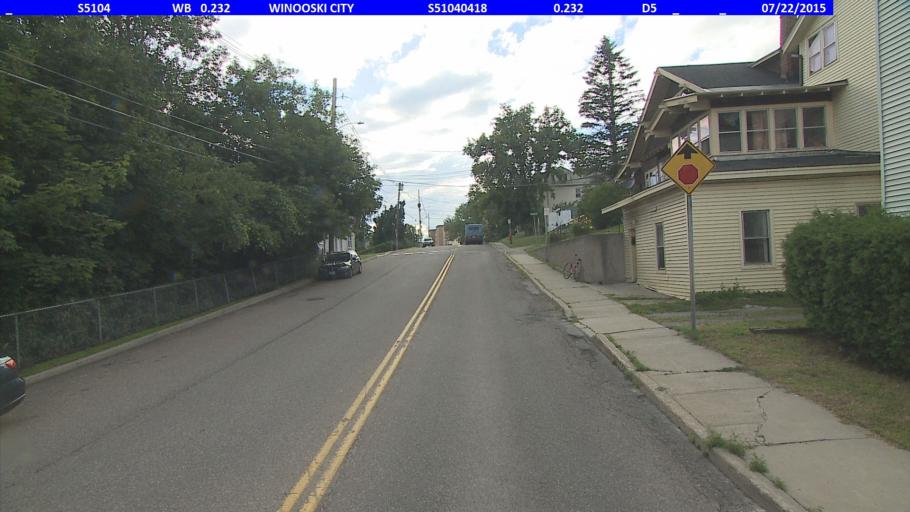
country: US
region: Vermont
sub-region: Chittenden County
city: Winooski
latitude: 44.4936
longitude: -73.1816
